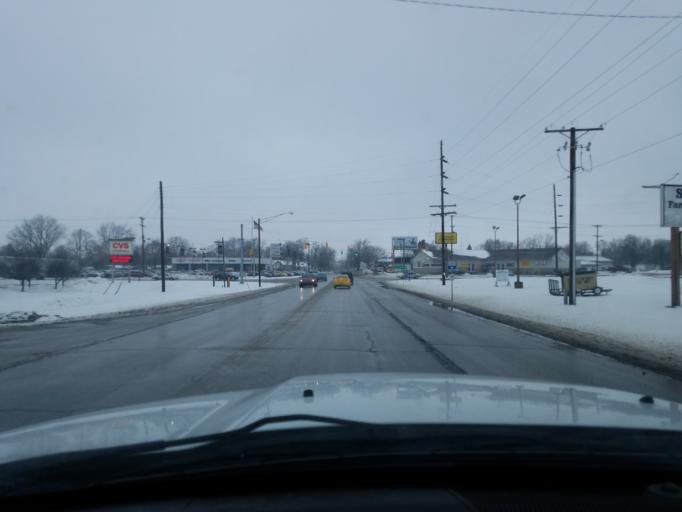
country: US
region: Indiana
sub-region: Fulton County
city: Rochester
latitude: 41.0541
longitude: -86.2177
